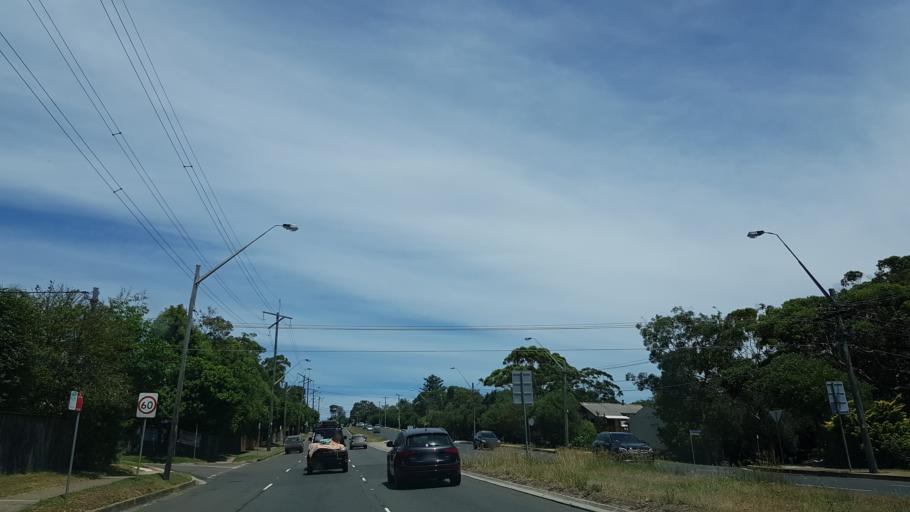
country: AU
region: New South Wales
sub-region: Pittwater
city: Newport
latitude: -33.6594
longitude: 151.3171
